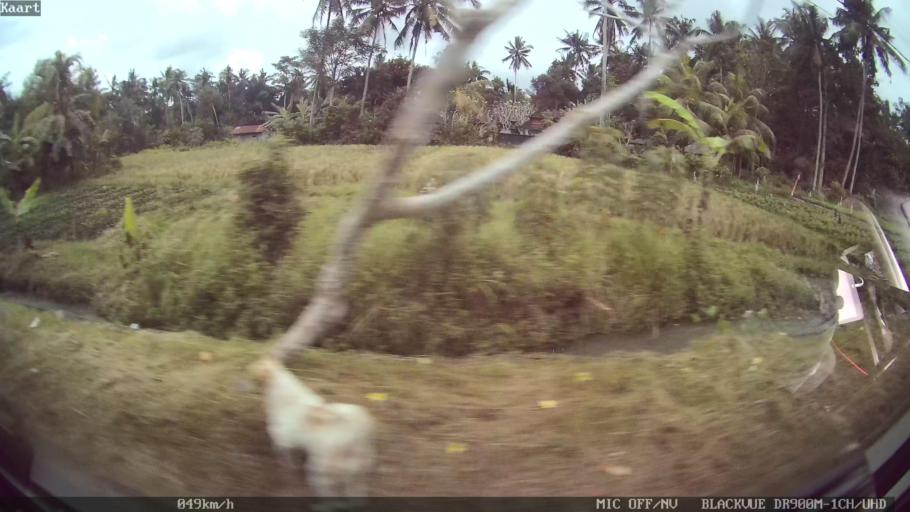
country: ID
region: Bali
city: Banjar Serangan
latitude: -8.5280
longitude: 115.1805
